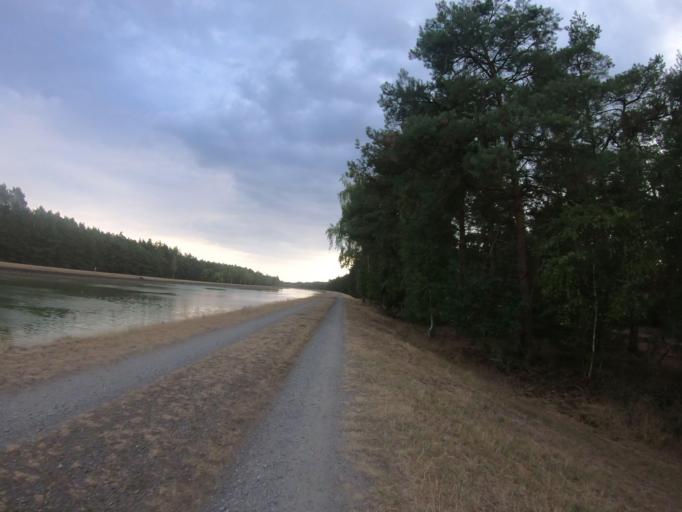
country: DE
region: Lower Saxony
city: Sassenburg
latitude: 52.5376
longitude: 10.6570
